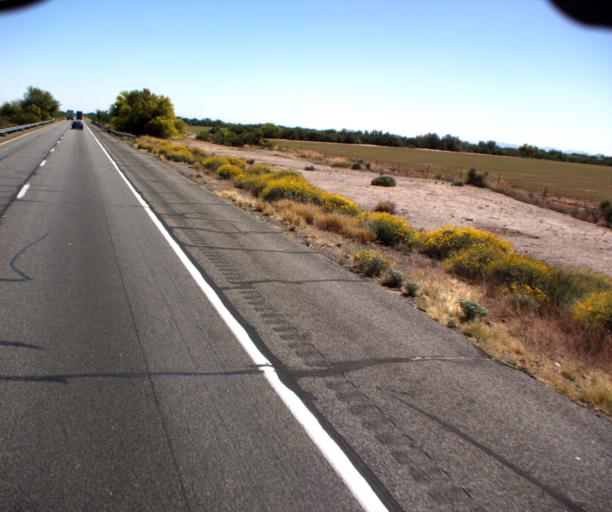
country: US
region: Arizona
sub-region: Maricopa County
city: Buckeye
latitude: 33.4888
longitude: -112.8992
